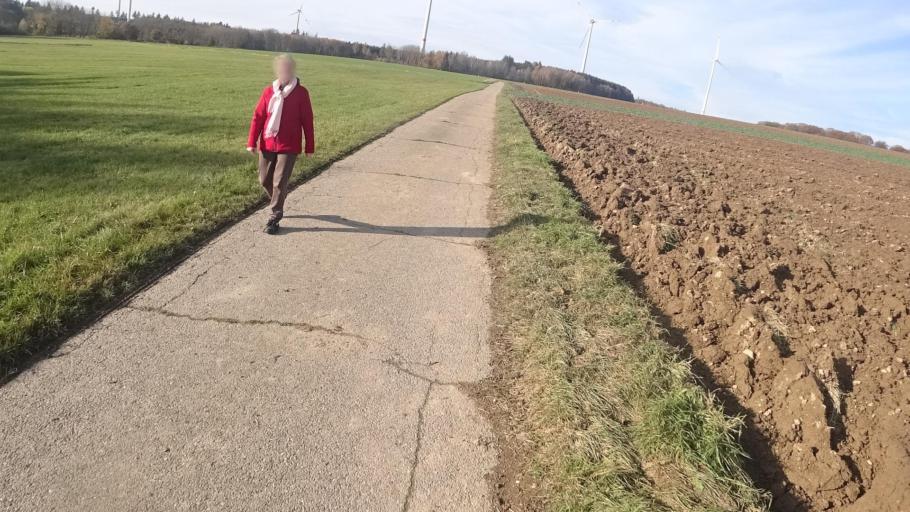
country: DE
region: Rheinland-Pfalz
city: Hausbay
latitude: 50.1057
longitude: 7.5521
